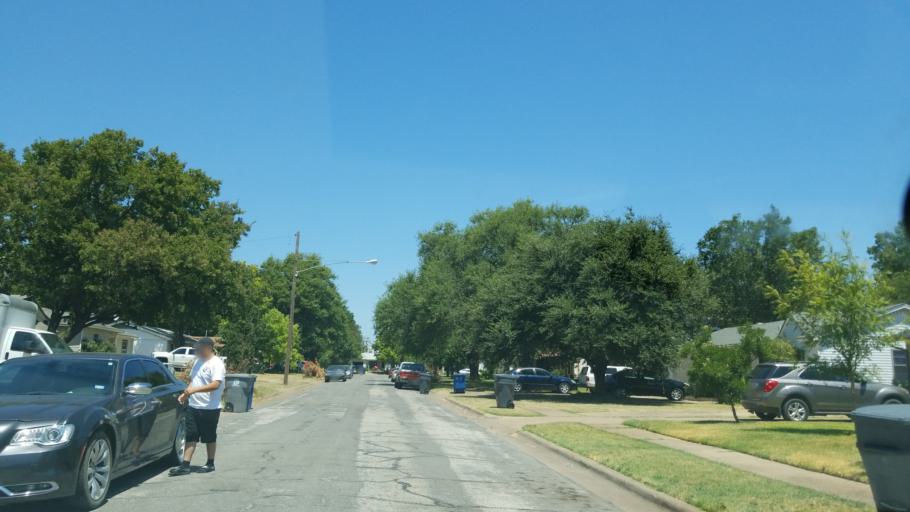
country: US
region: Texas
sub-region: Dallas County
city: Cockrell Hill
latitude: 32.7325
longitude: -96.8836
